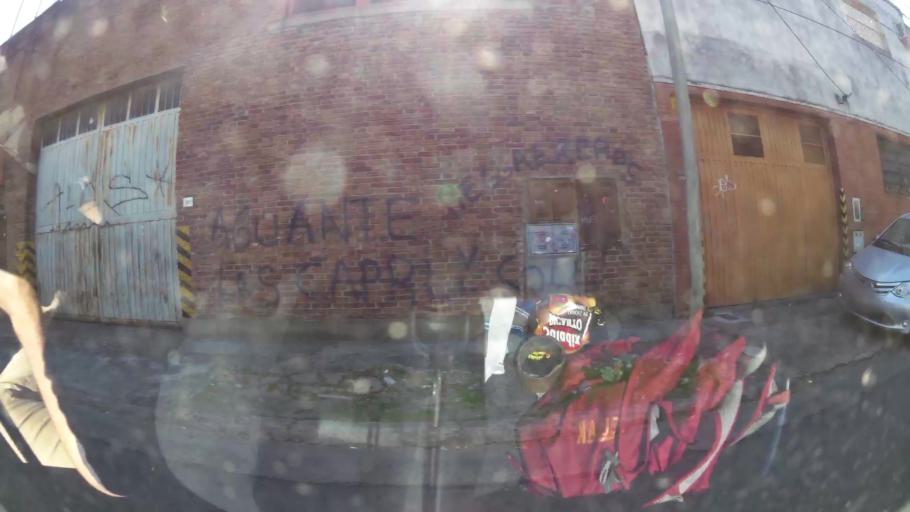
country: AR
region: Buenos Aires
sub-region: Partido de General San Martin
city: General San Martin
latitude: -34.5405
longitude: -58.5383
